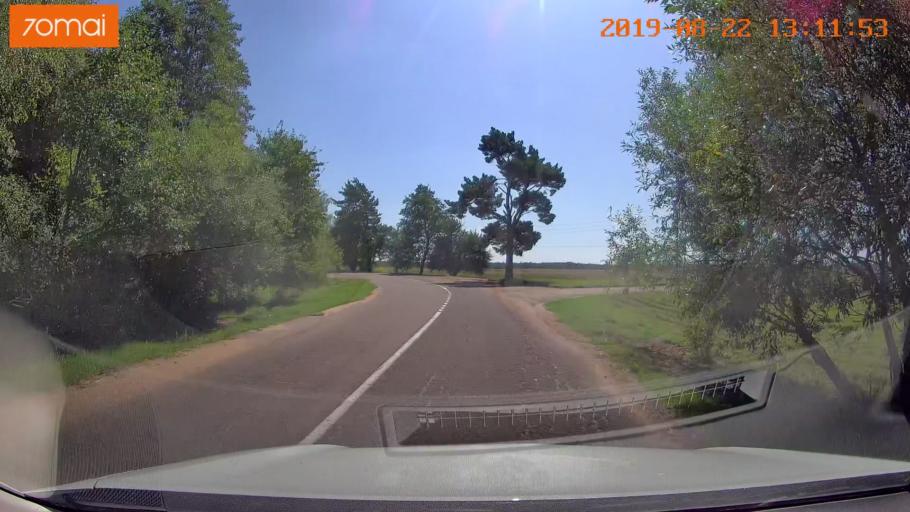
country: BY
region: Minsk
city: Prawdzinski
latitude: 53.2740
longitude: 27.8549
